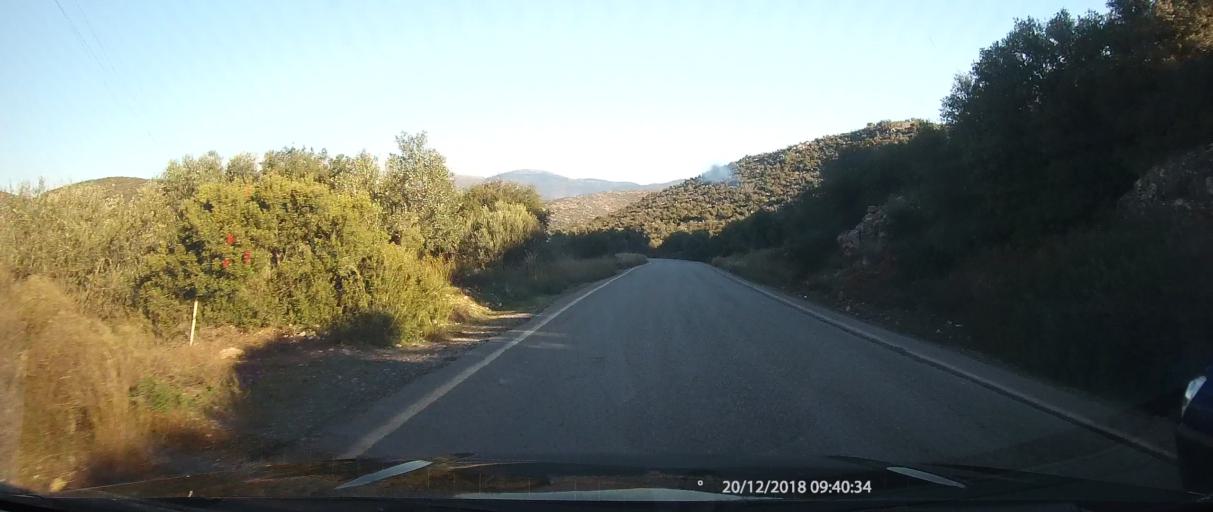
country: GR
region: Peloponnese
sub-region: Nomos Lakonias
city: Yerakion
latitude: 36.9450
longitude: 22.7667
